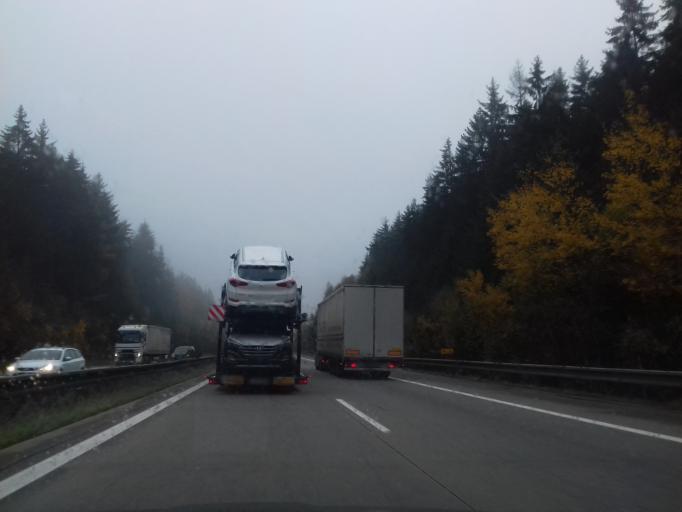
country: CZ
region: Vysocina
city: Vilemov
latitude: 49.5188
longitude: 15.3938
